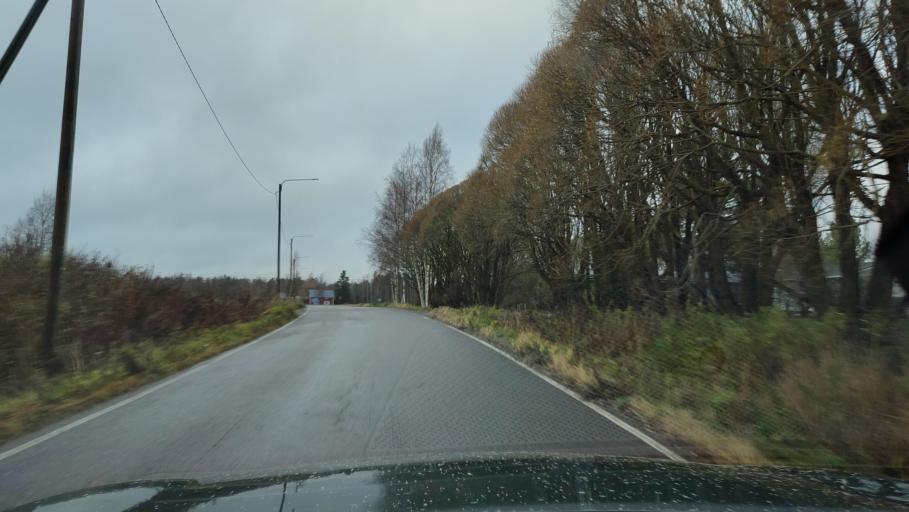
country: FI
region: Southern Ostrobothnia
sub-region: Suupohja
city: Teuva
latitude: 62.4503
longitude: 21.6037
